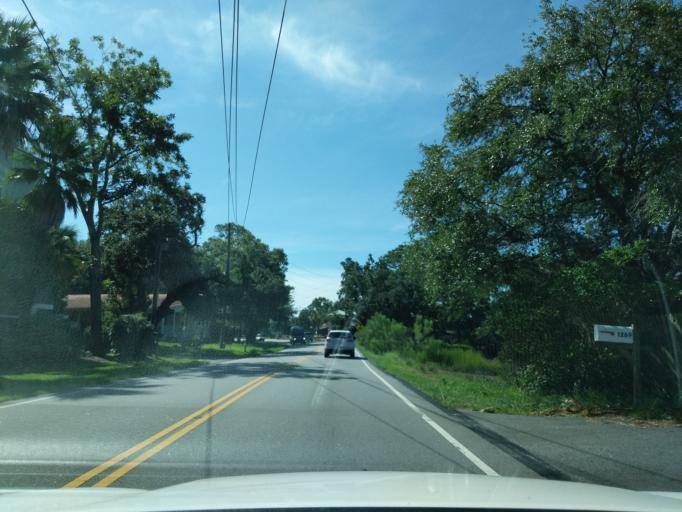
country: US
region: South Carolina
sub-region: Charleston County
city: Charleston
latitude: 32.7524
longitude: -79.9533
